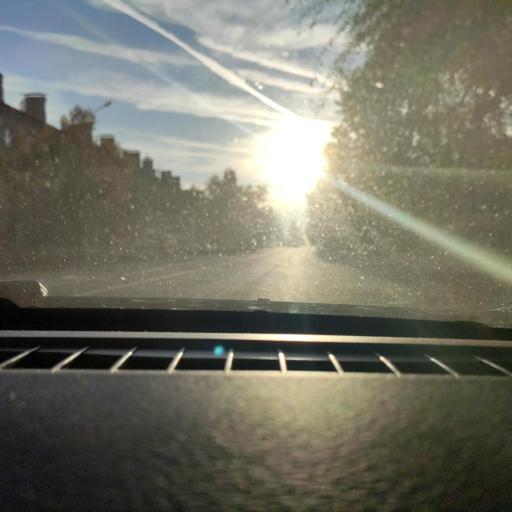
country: RU
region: Voronezj
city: Maslovka
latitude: 51.6199
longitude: 39.2480
